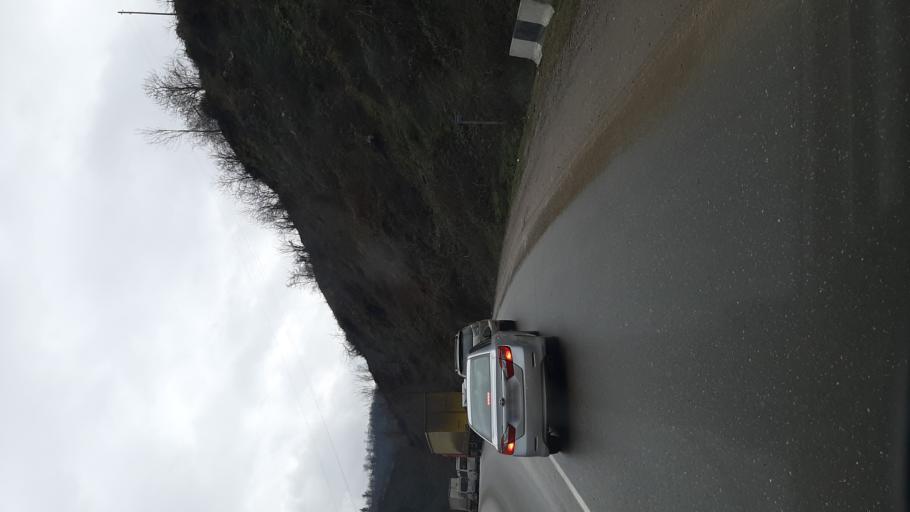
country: GE
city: Shorapani
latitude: 42.1049
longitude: 43.1675
